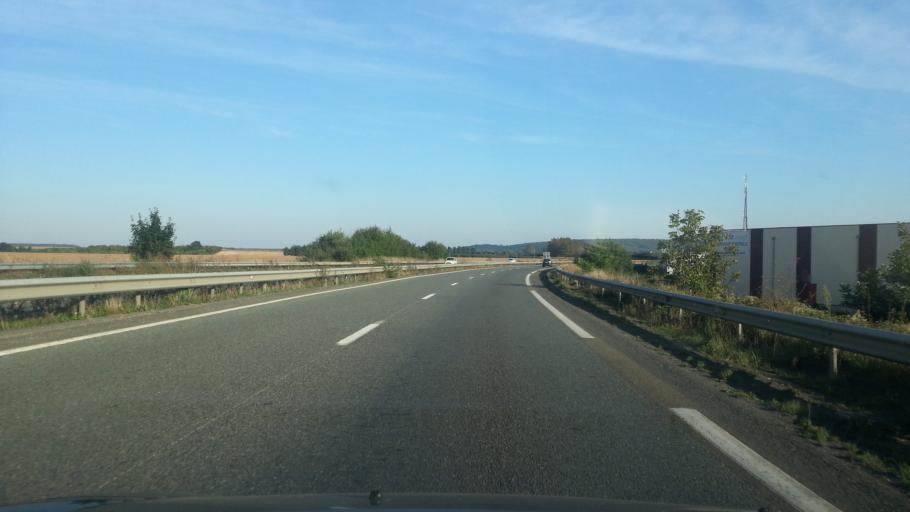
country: FR
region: Picardie
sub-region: Departement de l'Oise
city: Bresles
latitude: 49.4179
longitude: 2.2551
